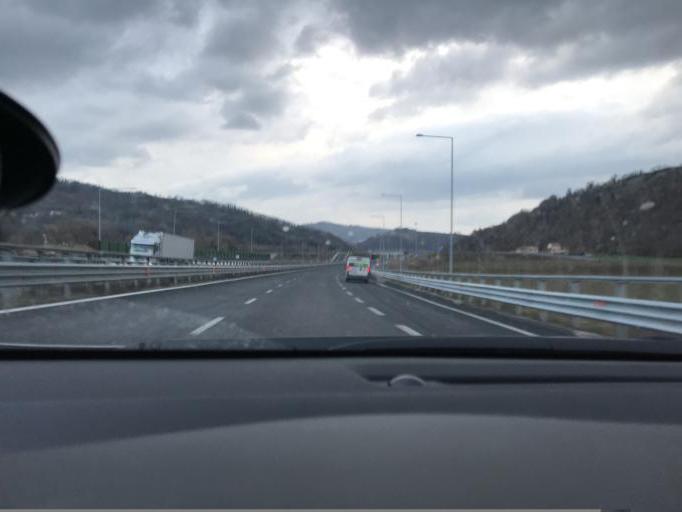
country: IT
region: Umbria
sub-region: Provincia di Perugia
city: Valfabbrica
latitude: 43.1602
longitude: 12.5941
